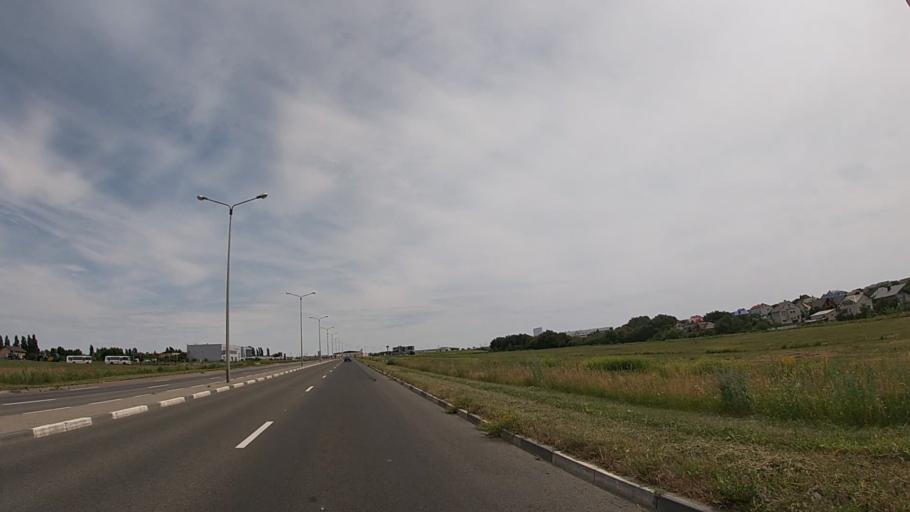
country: RU
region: Belgorod
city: Severnyy
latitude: 50.6568
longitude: 36.5460
